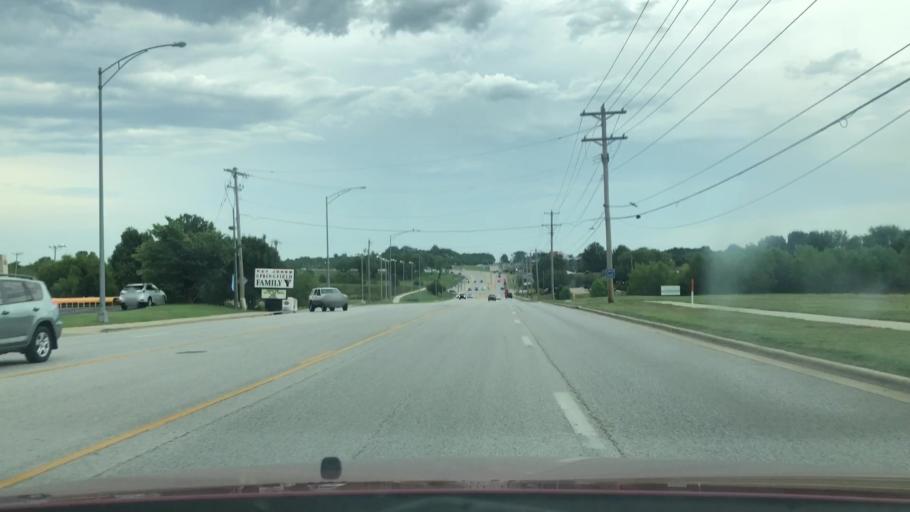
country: US
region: Missouri
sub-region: Greene County
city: Springfield
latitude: 37.1373
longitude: -93.2622
